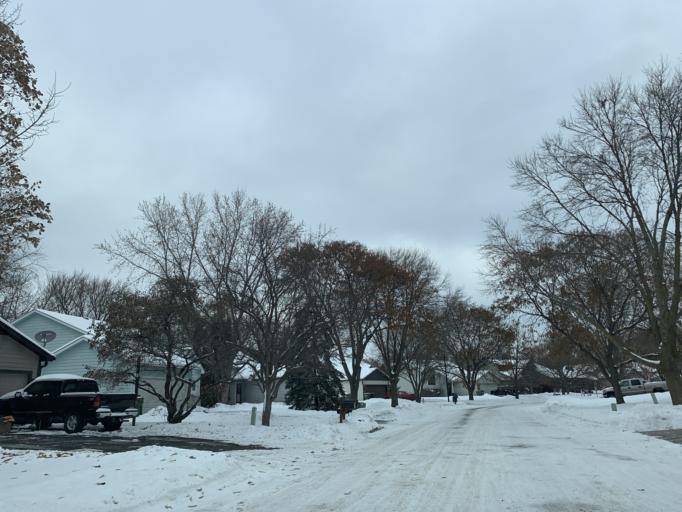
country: US
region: Minnesota
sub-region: Anoka County
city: Coon Rapids
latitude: 45.1656
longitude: -93.2846
